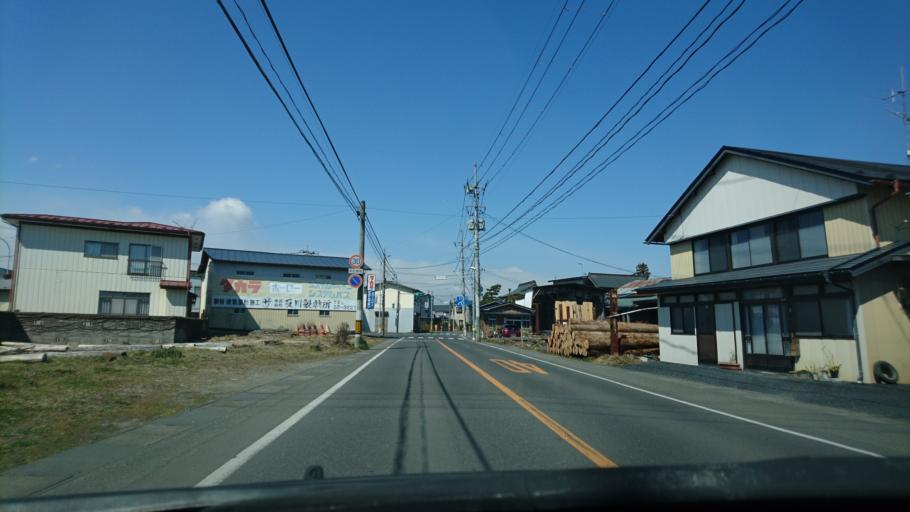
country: JP
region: Iwate
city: Ichinoseki
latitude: 38.7721
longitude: 141.1407
